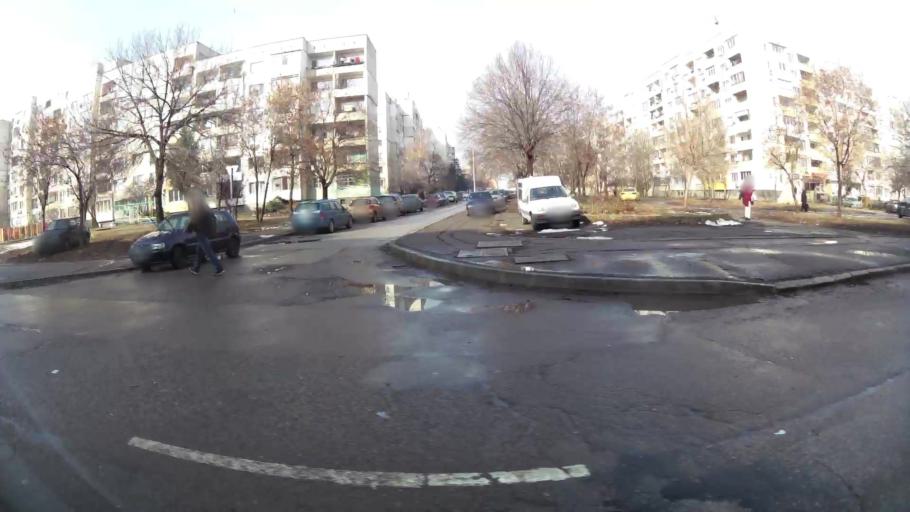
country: BG
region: Sofia-Capital
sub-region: Stolichna Obshtina
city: Sofia
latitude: 42.7187
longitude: 23.2624
